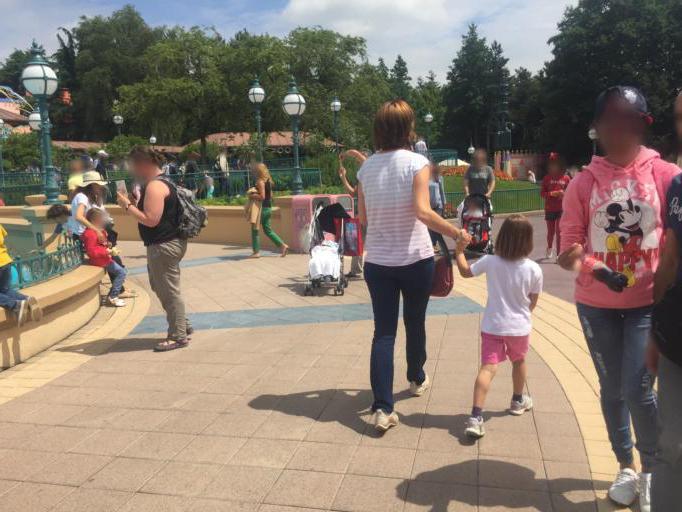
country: FR
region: Ile-de-France
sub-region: Departement de Seine-et-Marne
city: Chessy
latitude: 48.8745
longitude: 2.7760
